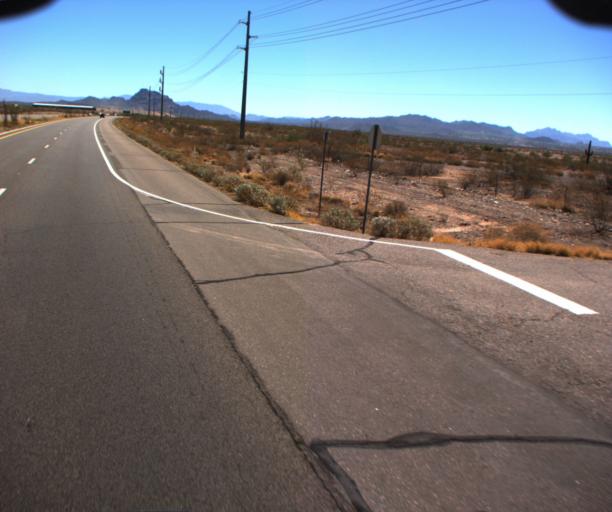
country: US
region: Arizona
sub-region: Maricopa County
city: Mesa
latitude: 33.5012
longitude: -111.7963
